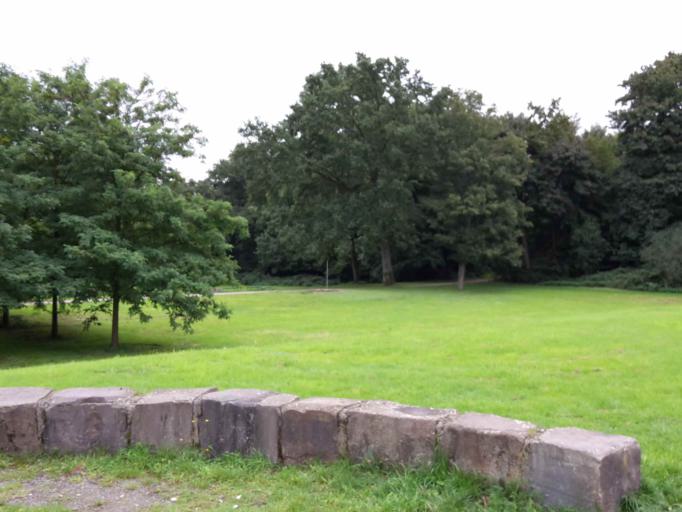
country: DE
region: North Rhine-Westphalia
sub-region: Regierungsbezirk Koln
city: Muelheim
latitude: 50.9920
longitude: 6.9958
